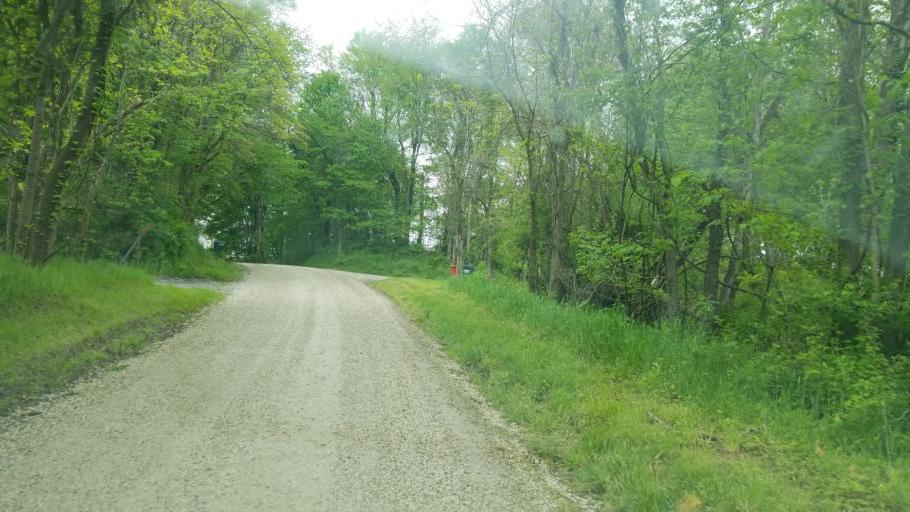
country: US
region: Ohio
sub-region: Tuscarawas County
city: Rockford
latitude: 40.4351
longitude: -81.2383
